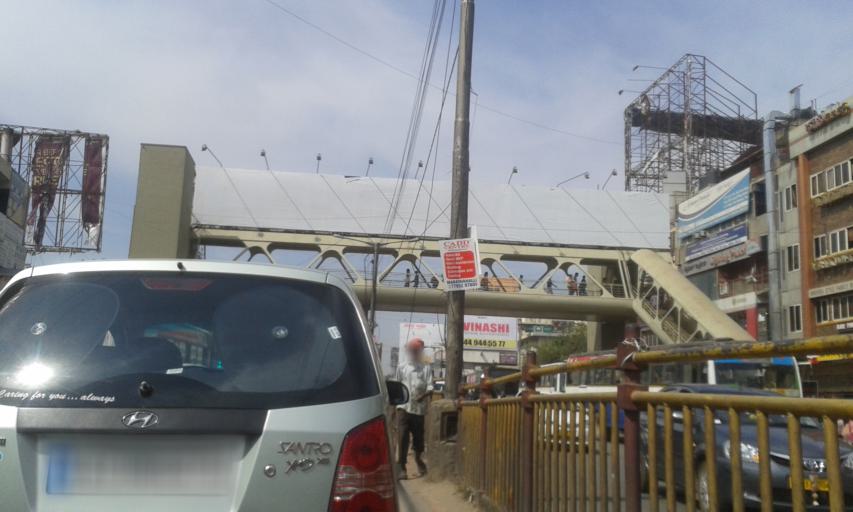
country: IN
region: Karnataka
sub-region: Bangalore Urban
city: Bangalore
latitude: 12.9568
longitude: 77.7022
